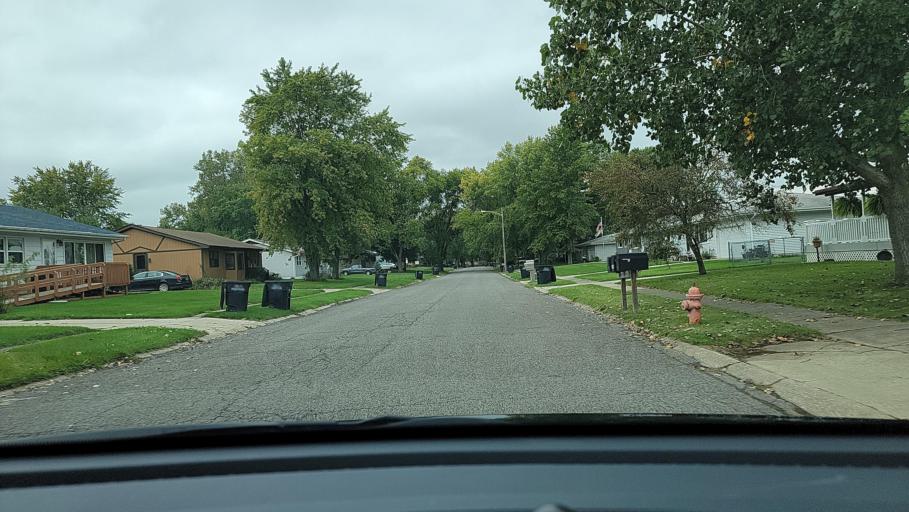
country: US
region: Indiana
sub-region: Porter County
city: Portage
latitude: 41.5600
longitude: -87.1985
